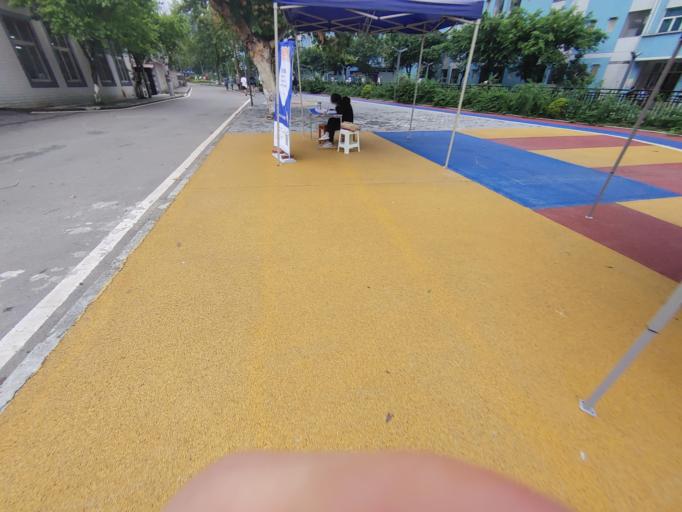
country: CN
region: Chongqing Shi
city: Shuangfeng
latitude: 29.9698
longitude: 106.4159
